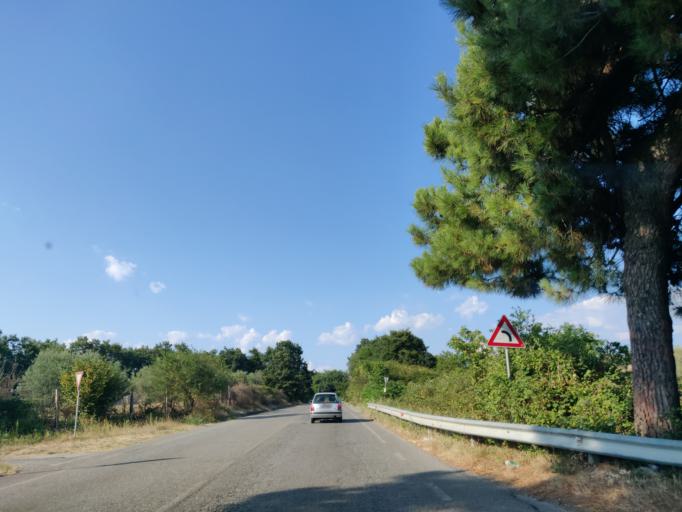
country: IT
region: Latium
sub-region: Provincia di Viterbo
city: Valentano
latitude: 42.5903
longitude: 11.8367
